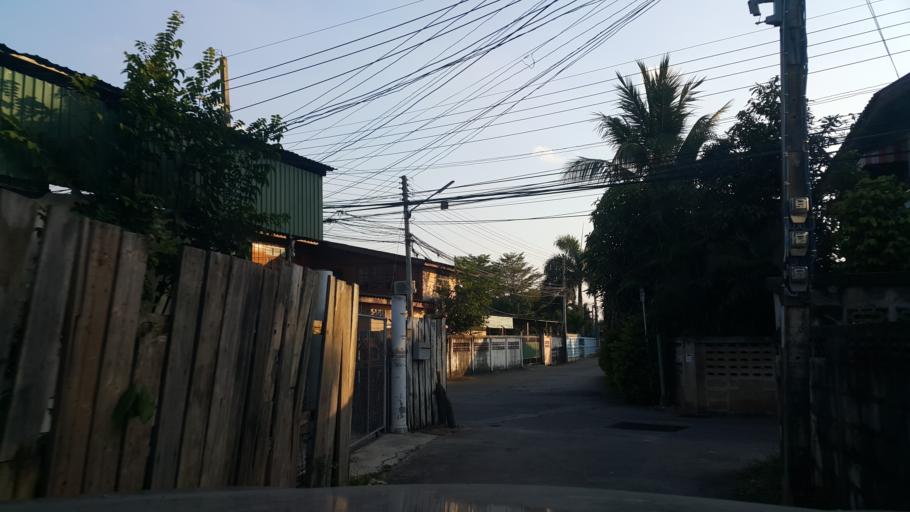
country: TH
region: Lampang
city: Lampang
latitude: 18.2769
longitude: 99.4683
